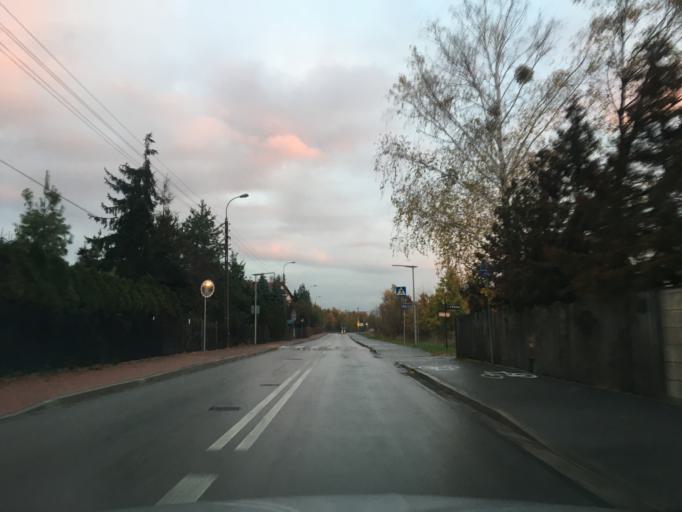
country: PL
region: Masovian Voivodeship
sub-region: Powiat pruszkowski
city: Brwinow
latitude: 52.1440
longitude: 20.7293
